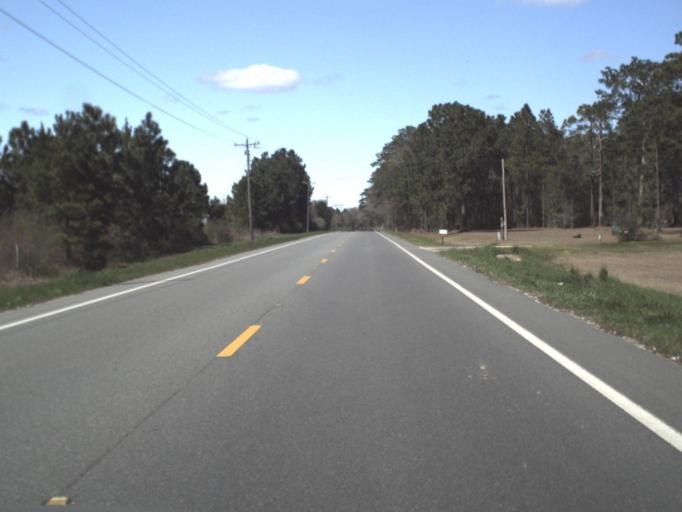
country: US
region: Florida
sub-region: Gadsden County
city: Gretna
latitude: 30.6430
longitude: -84.6775
